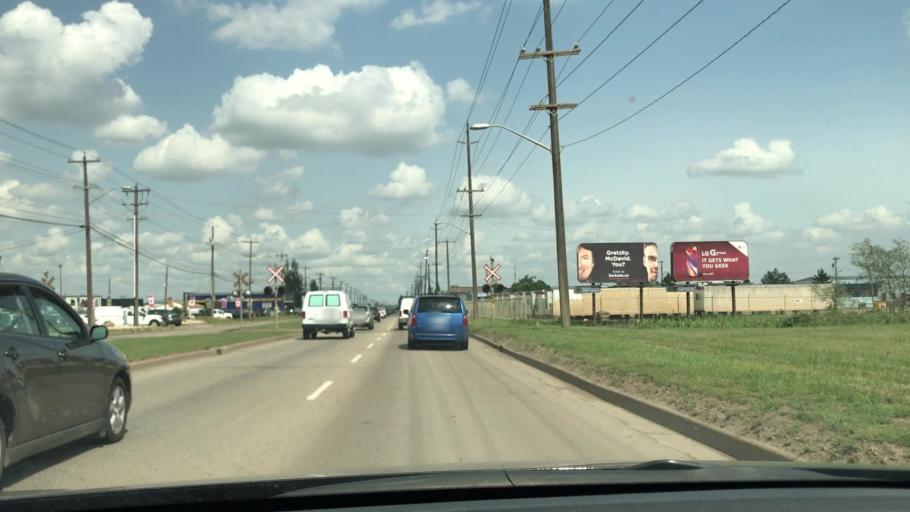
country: CA
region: Alberta
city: Edmonton
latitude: 53.5064
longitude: -113.4182
